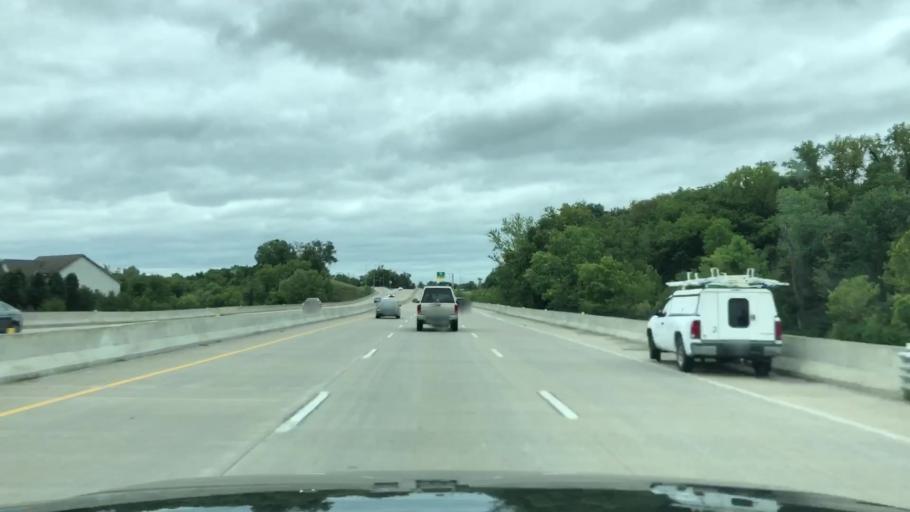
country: US
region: Missouri
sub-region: Saint Louis County
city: Maryland Heights
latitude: 38.6875
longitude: -90.4954
